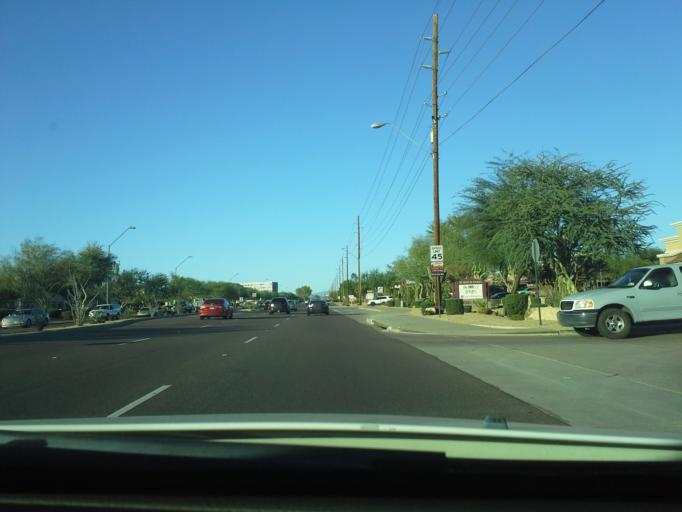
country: US
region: Arizona
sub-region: Maricopa County
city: Paradise Valley
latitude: 33.6265
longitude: -111.9254
